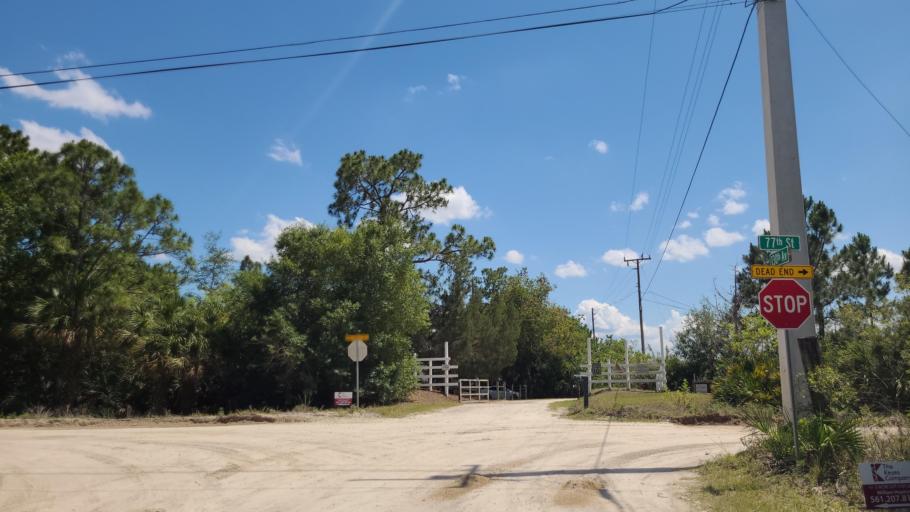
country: US
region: Florida
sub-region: Indian River County
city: Fellsmere
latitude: 27.7358
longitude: -80.5936
